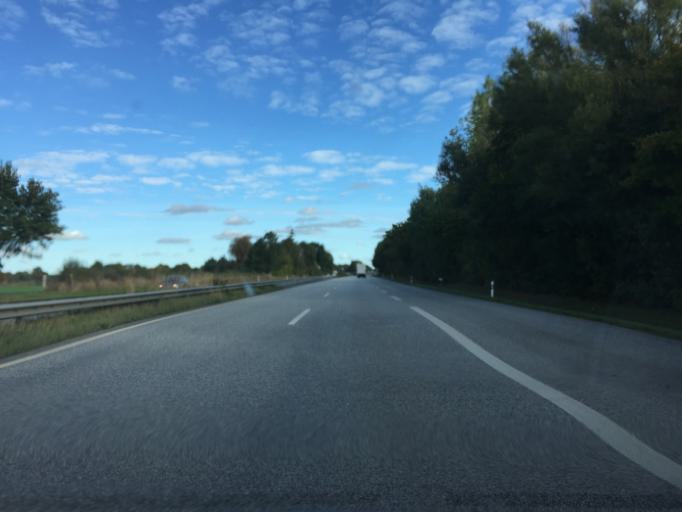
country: DE
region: Schleswig-Holstein
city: Beschendorf
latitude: 54.1557
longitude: 10.8568
